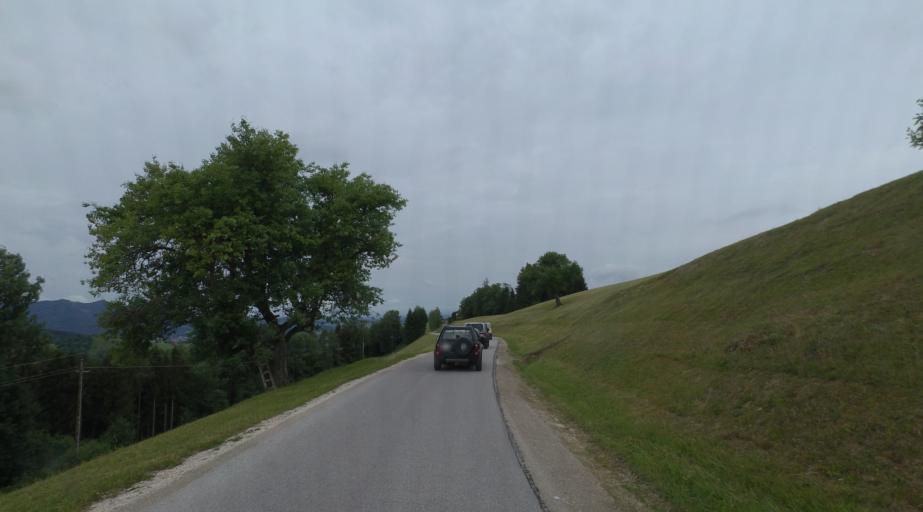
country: AT
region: Upper Austria
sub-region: Politischer Bezirk Kirchdorf an der Krems
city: Micheldorf in Oberoesterreich
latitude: 47.9365
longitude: 14.1662
